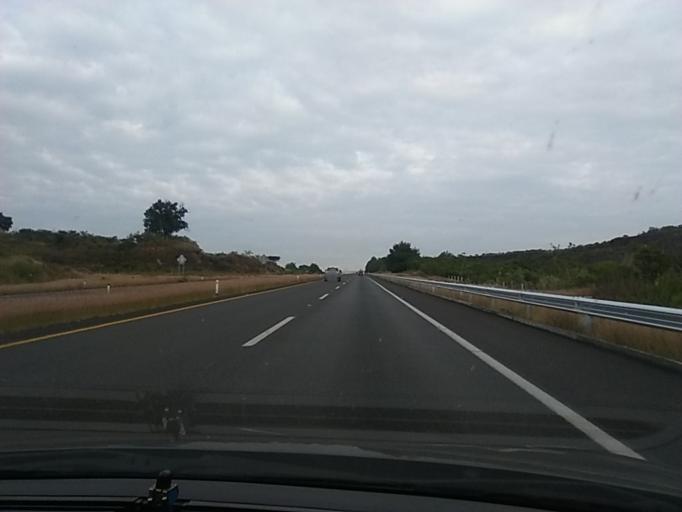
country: MX
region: Michoacan
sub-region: Puruandiro
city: San Lorenzo
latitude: 19.9603
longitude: -101.6841
